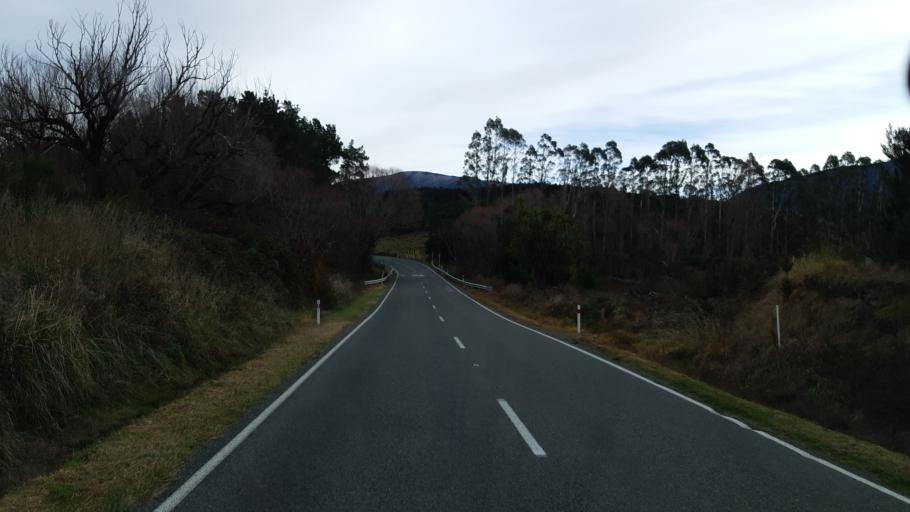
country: NZ
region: Tasman
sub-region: Tasman District
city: Brightwater
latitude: -41.6573
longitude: 173.2342
